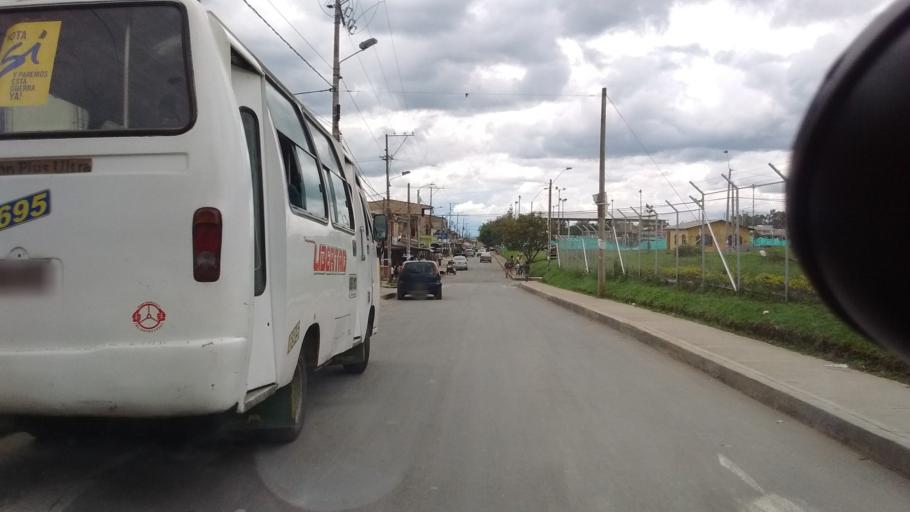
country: CO
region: Cauca
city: Popayan
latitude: 2.4749
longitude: -76.5585
